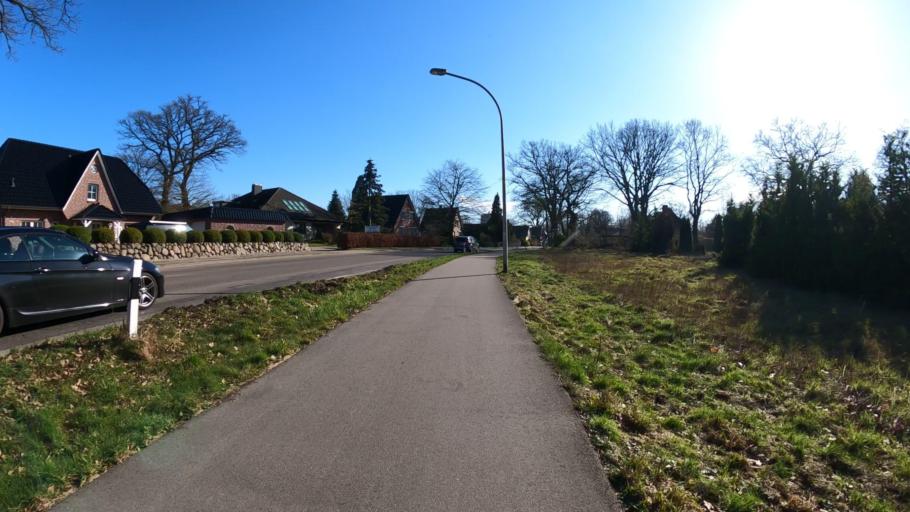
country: DE
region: Schleswig-Holstein
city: Rellingen
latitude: 53.6238
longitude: 9.7984
